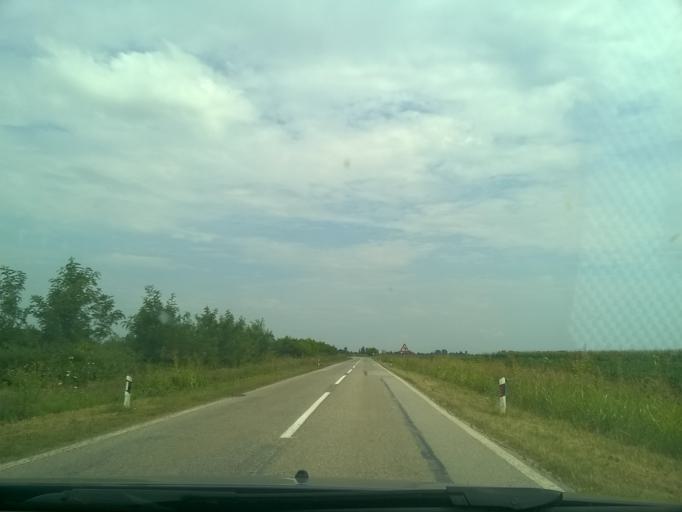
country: RS
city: Velika Greda
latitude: 45.2317
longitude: 21.0058
